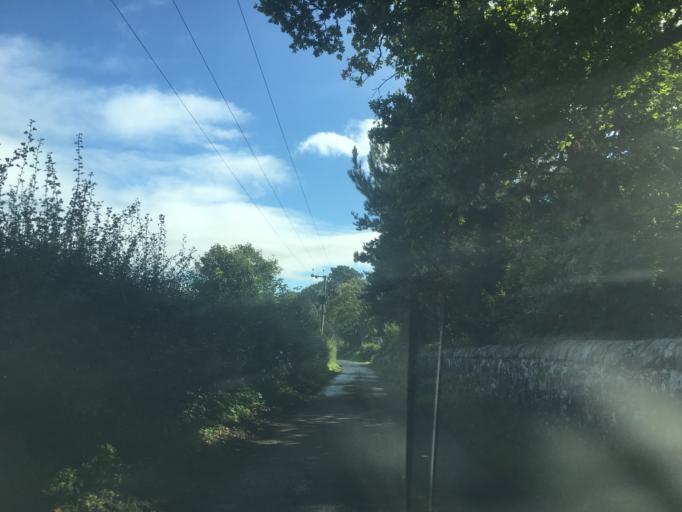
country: GB
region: Scotland
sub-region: Edinburgh
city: Kirkliston
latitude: 55.9560
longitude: -3.3733
